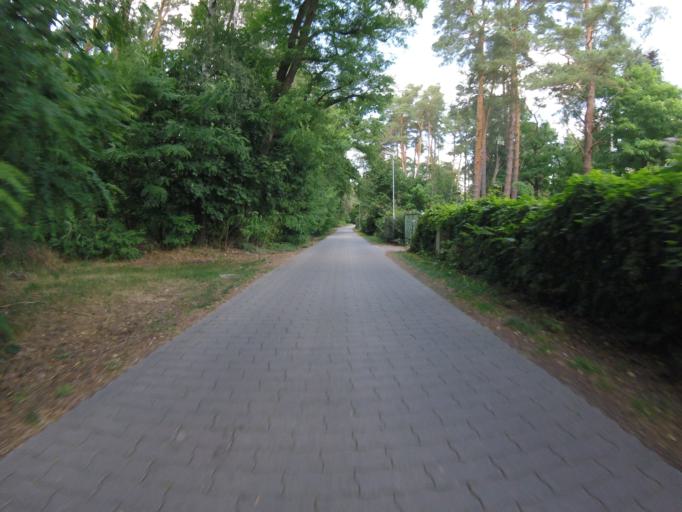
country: DE
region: Brandenburg
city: Bestensee
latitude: 52.2519
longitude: 13.6456
